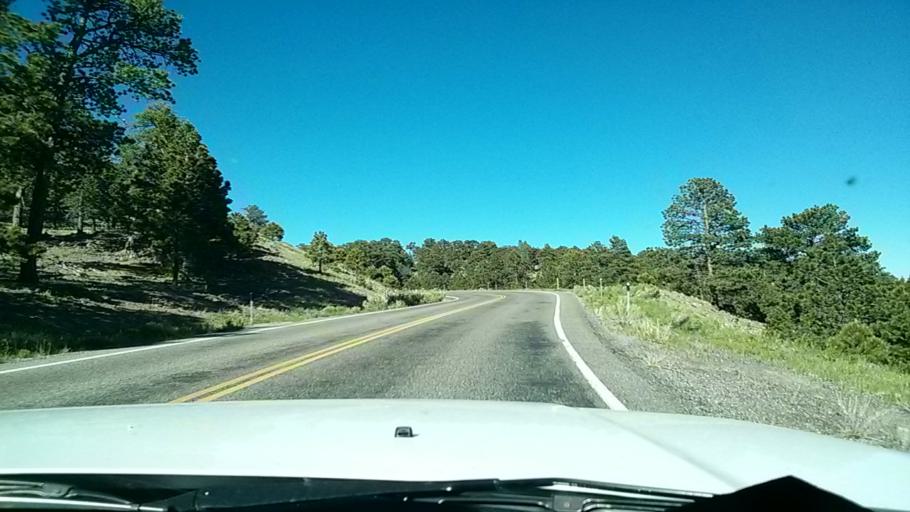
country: US
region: Utah
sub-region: Wayne County
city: Loa
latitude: 38.1166
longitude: -111.3291
